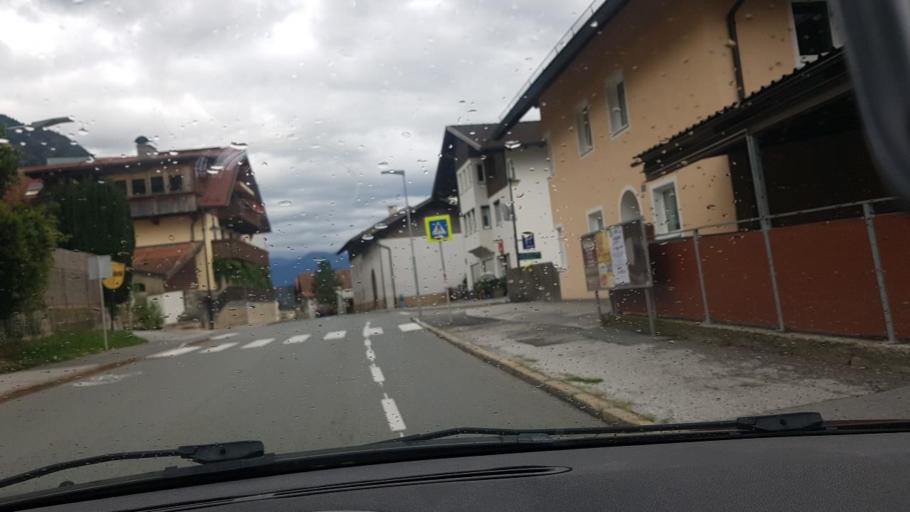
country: AT
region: Tyrol
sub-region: Politischer Bezirk Innsbruck Land
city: Zirl
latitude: 47.2741
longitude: 11.2393
